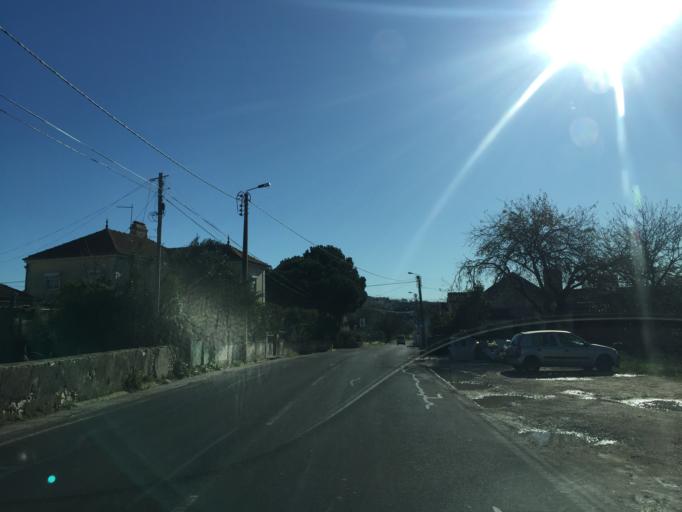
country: PT
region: Lisbon
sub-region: Sintra
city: Pero Pinheiro
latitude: 38.8301
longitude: -9.3039
